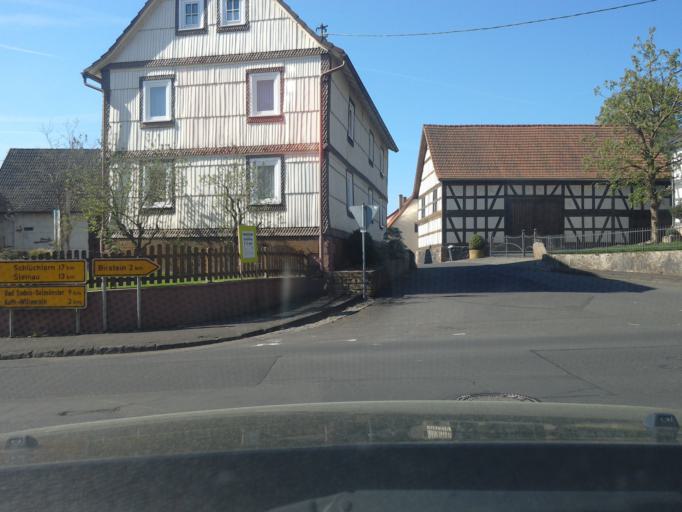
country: DE
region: Hesse
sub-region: Regierungsbezirk Darmstadt
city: Birstein
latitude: 50.3395
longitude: 9.3227
